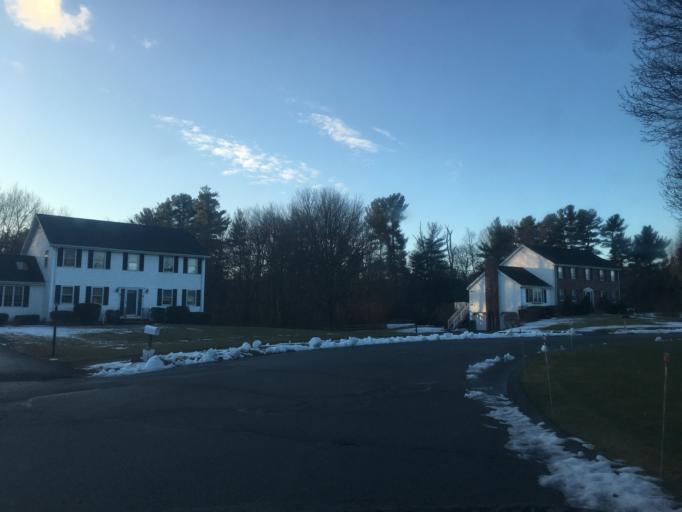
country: US
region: Massachusetts
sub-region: Middlesex County
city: Pinehurst
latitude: 42.5456
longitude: -71.2411
